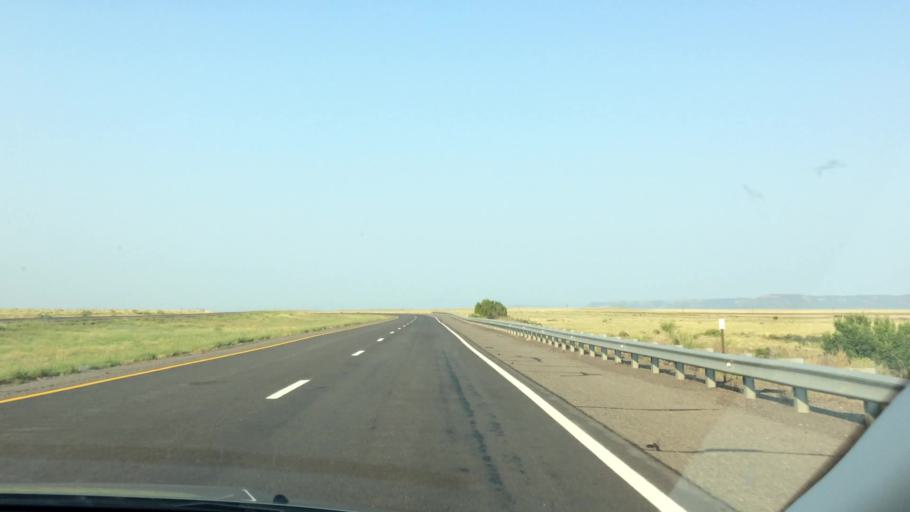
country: US
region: New Mexico
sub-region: Colfax County
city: Raton
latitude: 36.7227
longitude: -104.4688
